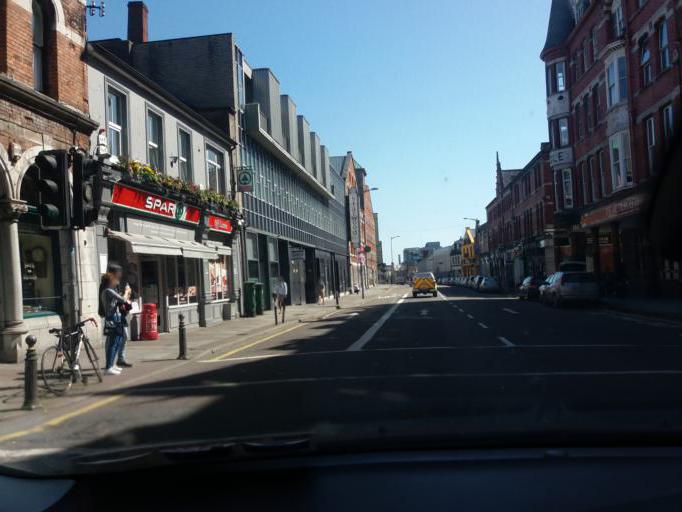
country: IE
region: Munster
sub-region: County Cork
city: Cork
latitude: 51.9015
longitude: -8.4680
